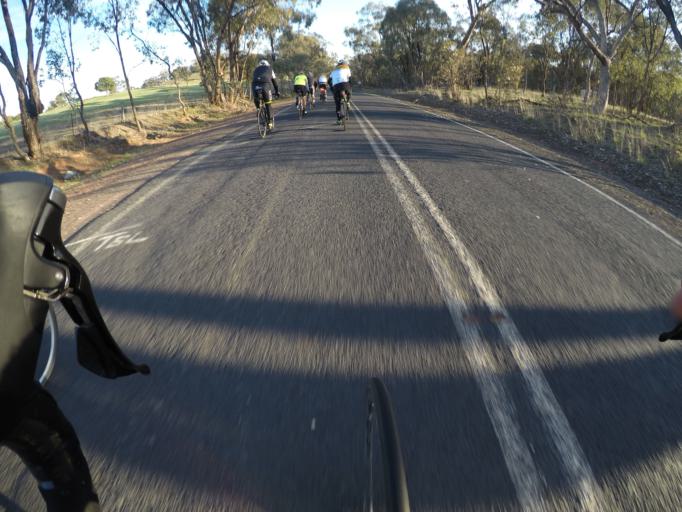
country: AU
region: New South Wales
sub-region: Cabonne
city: Molong
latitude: -33.0662
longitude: 148.8250
